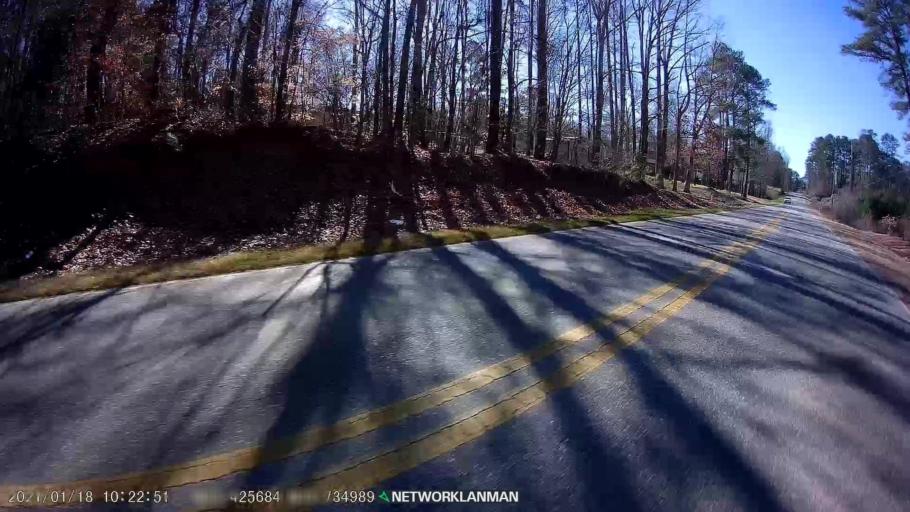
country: US
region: Georgia
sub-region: Haralson County
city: Tallapoosa
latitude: 33.7349
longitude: -85.4258
